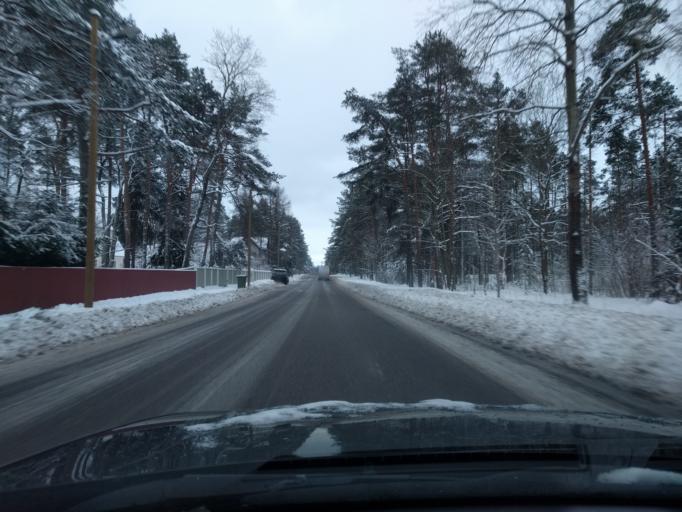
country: EE
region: Harju
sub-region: Saue vald
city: Laagri
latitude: 59.3774
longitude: 24.6705
